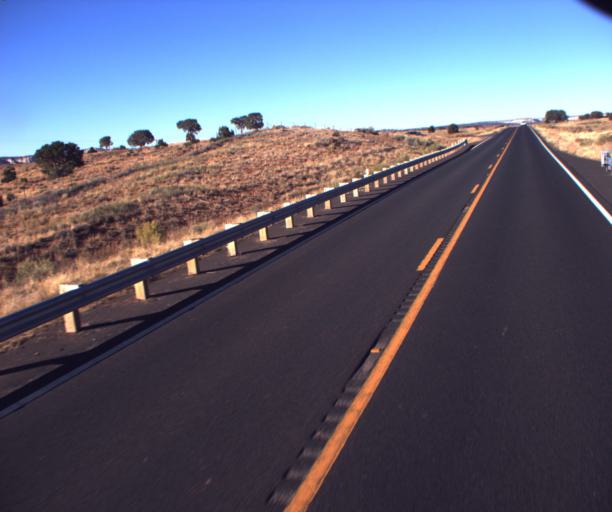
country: US
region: Arizona
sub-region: Apache County
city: Ganado
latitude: 35.7866
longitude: -109.6929
